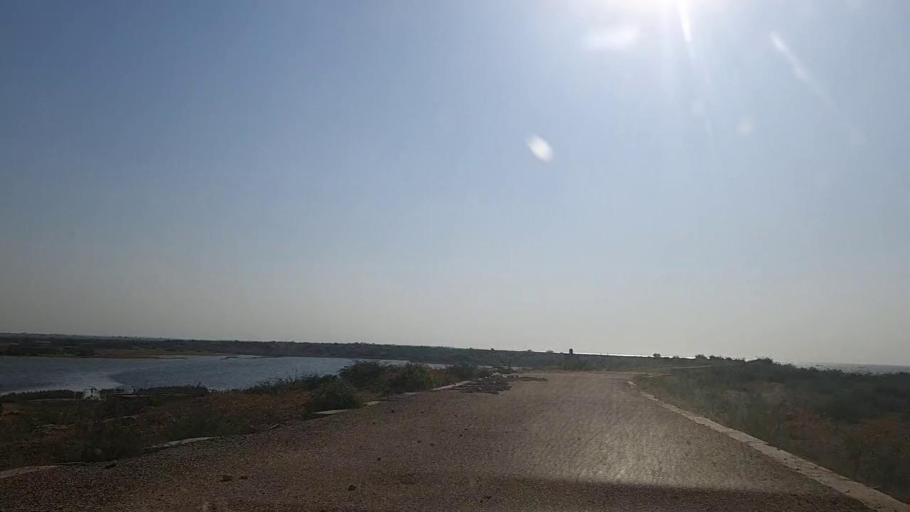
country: PK
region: Sindh
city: Daro Mehar
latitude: 25.0036
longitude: 68.1127
